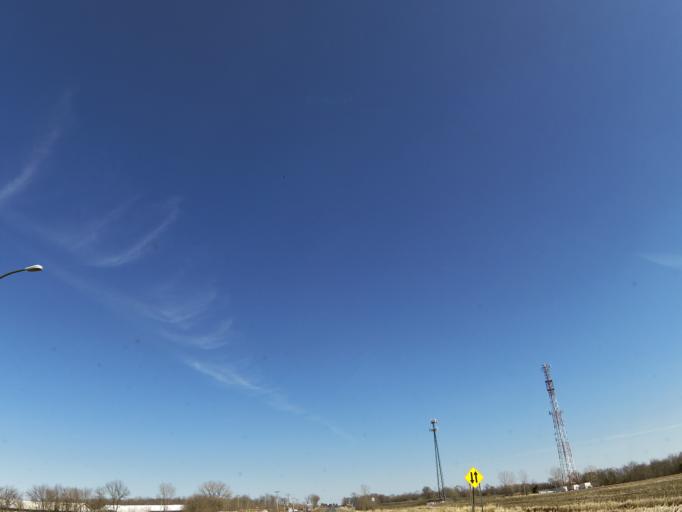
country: US
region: Minnesota
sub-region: Hennepin County
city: Medina
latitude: 45.0654
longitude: -93.6333
